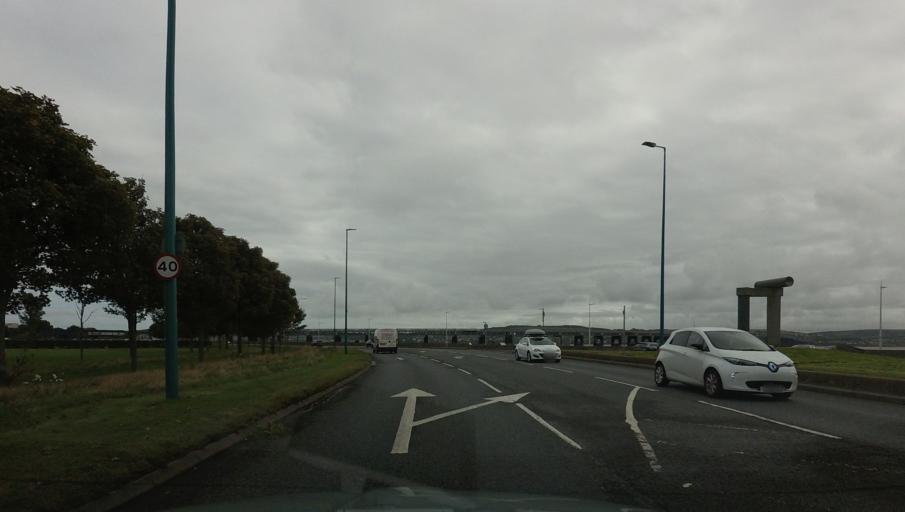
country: GB
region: Scotland
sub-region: Dundee City
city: Dundee
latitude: 56.4518
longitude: -2.9974
